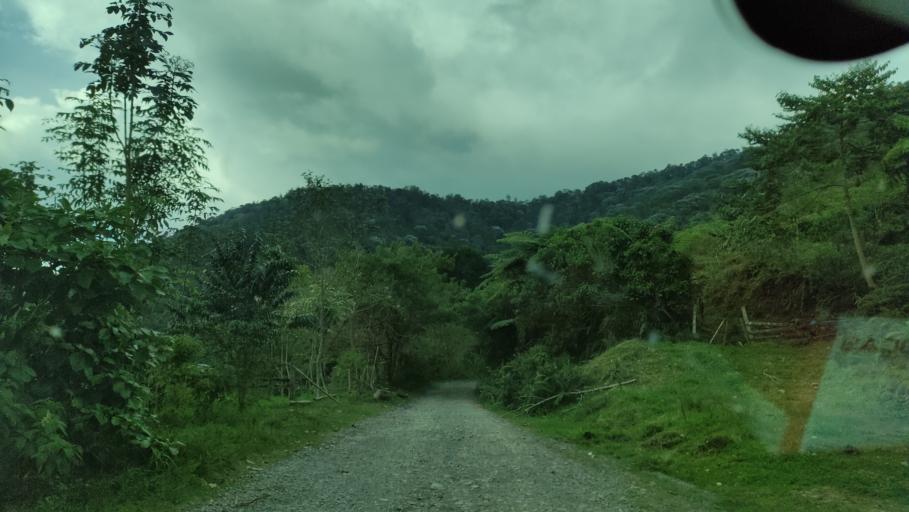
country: CO
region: Valle del Cauca
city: San Pedro
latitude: 3.8774
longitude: -76.1498
